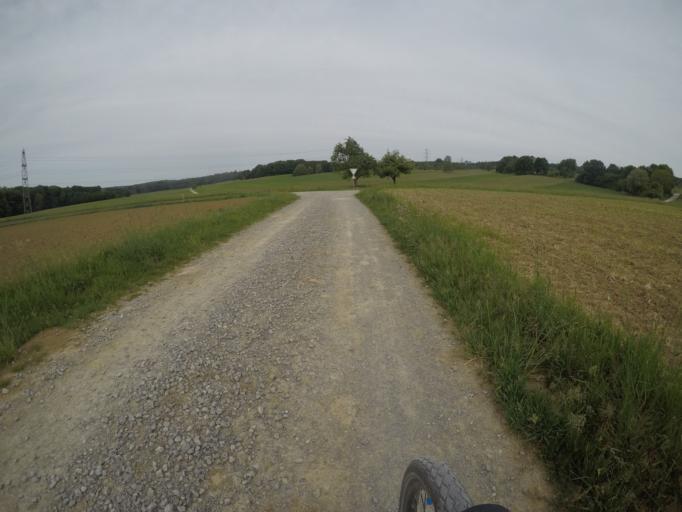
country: DE
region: Baden-Wuerttemberg
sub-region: Tuebingen Region
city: Kirchentellinsfurt
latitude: 48.5875
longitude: 9.1578
